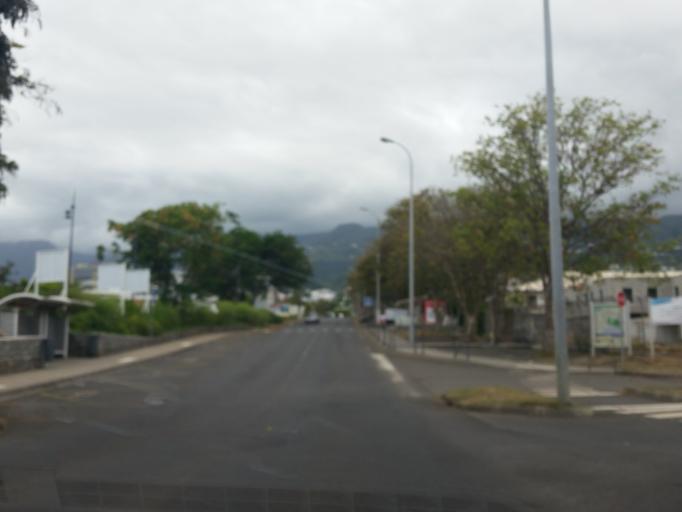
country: RE
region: Reunion
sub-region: Reunion
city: Saint-Denis
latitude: -20.8879
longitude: 55.4721
